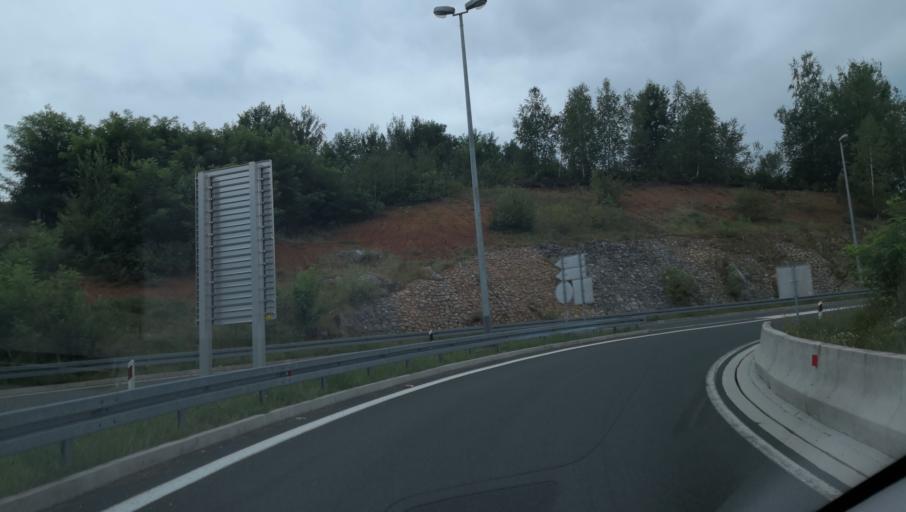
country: HR
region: Karlovacka
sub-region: Grad Karlovac
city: Karlovac
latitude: 45.4792
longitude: 15.4307
